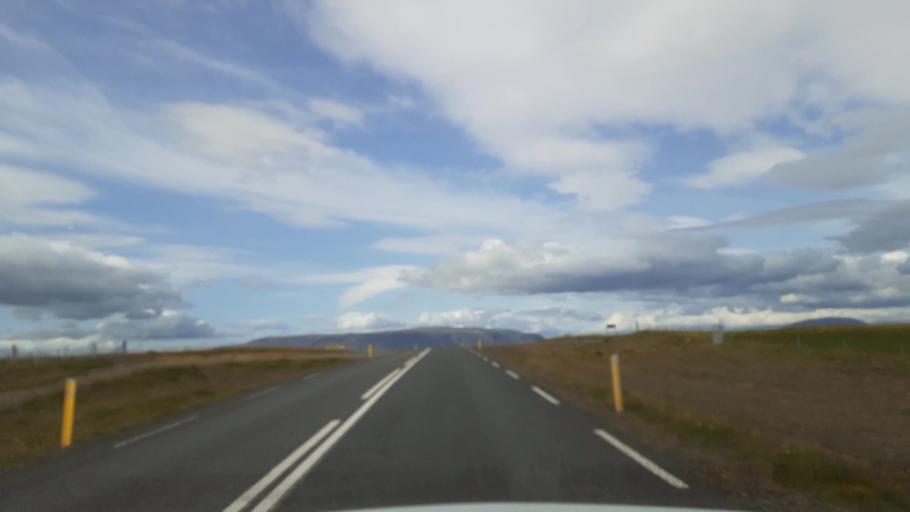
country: IS
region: South
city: Selfoss
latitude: 63.9034
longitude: -20.8130
